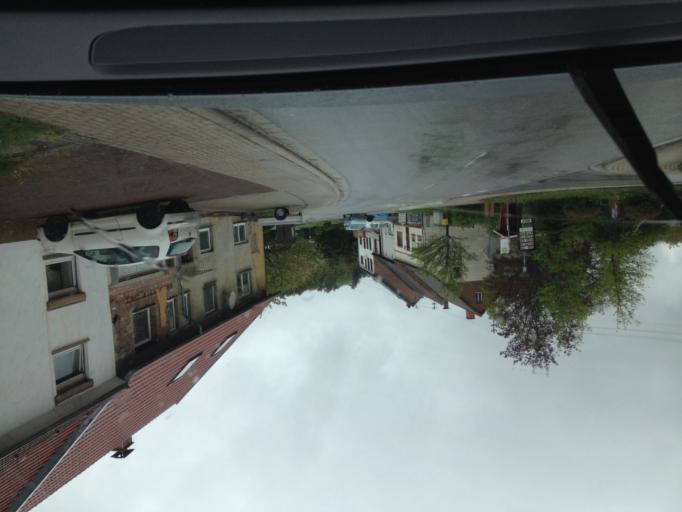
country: DE
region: Rheinland-Pfalz
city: Reichweiler
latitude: 49.5343
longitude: 7.2842
